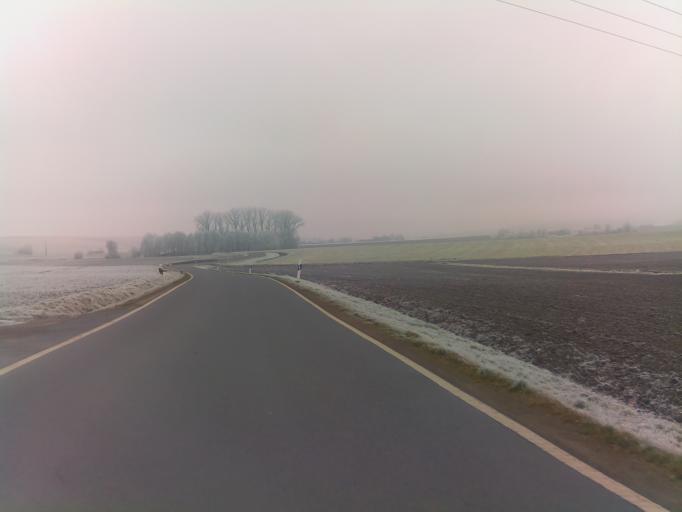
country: DE
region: Bavaria
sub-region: Regierungsbezirk Unterfranken
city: Butthard
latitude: 49.5760
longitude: 9.8612
